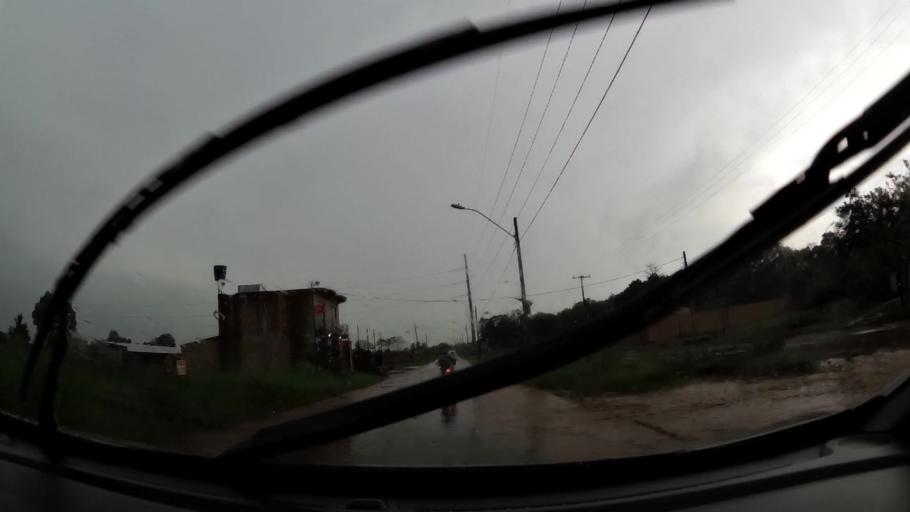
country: PY
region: Alto Parana
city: Presidente Franco
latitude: -25.5222
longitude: -54.6762
